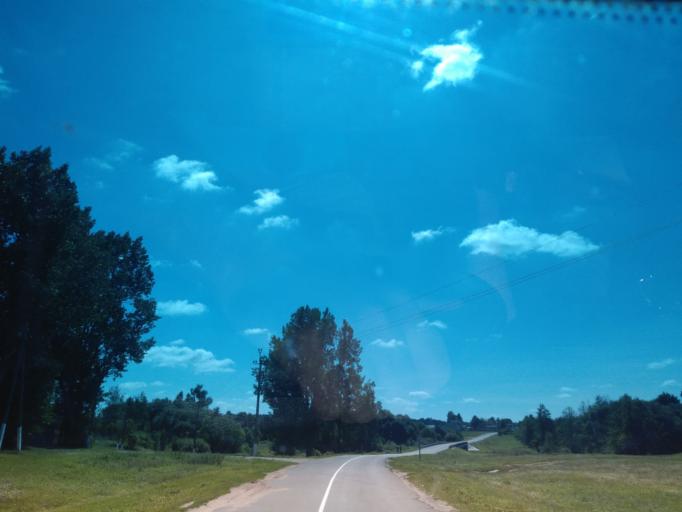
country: BY
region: Minsk
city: Kapyl'
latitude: 53.2561
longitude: 27.1832
